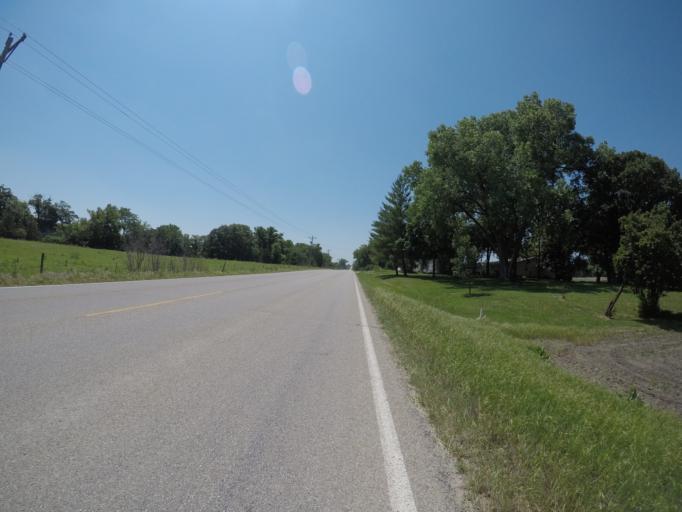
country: US
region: Kansas
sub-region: Pottawatomie County
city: Westmoreland
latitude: 39.2748
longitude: -96.4450
